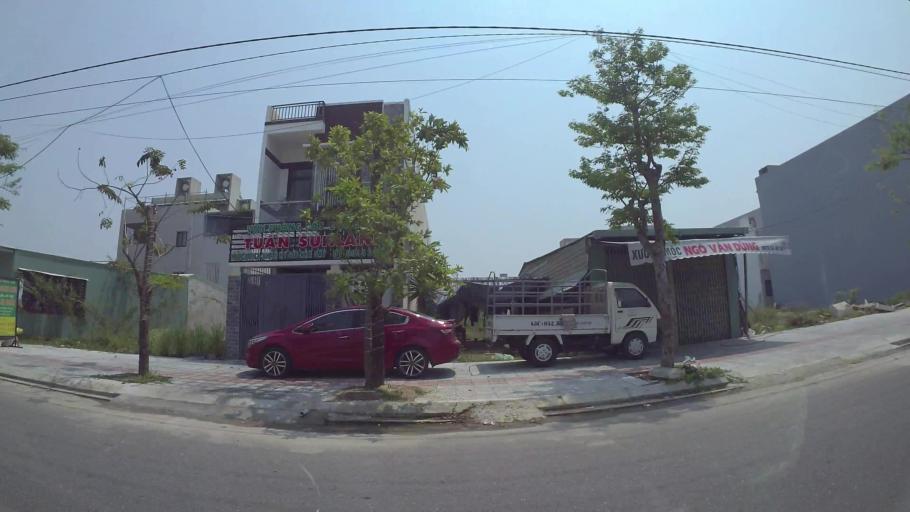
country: VN
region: Da Nang
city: Cam Le
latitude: 16.0136
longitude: 108.2208
